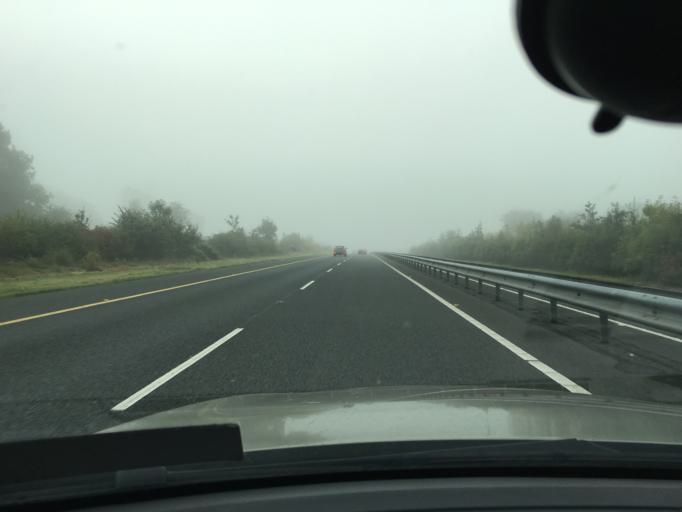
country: IE
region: Leinster
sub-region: An Iarmhi
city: Athlone
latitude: 53.3875
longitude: -8.0503
